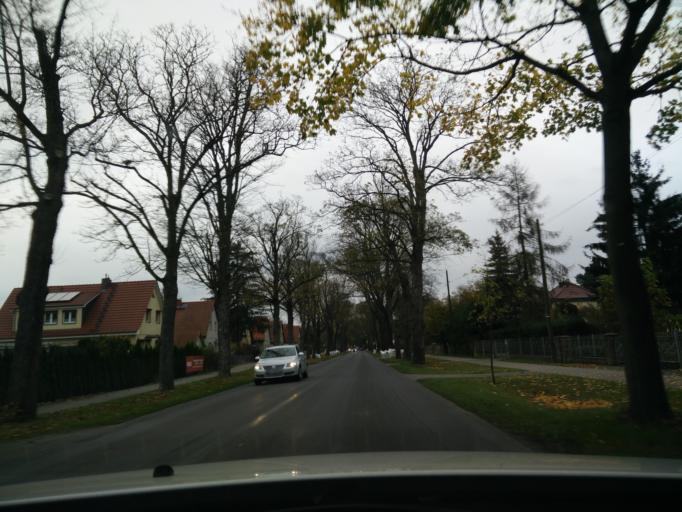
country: DE
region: Brandenburg
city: Falkensee
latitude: 52.5735
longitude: 13.0858
